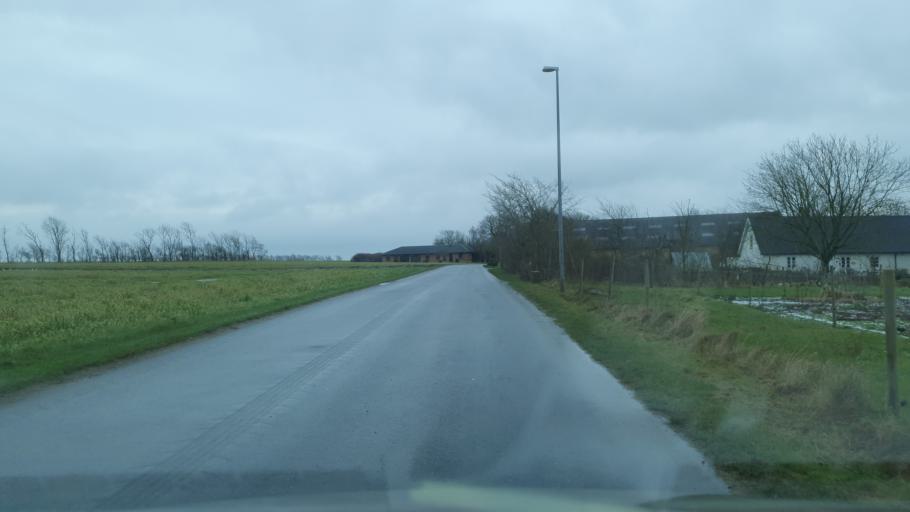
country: DK
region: North Denmark
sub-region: Jammerbugt Kommune
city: Fjerritslev
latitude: 57.1119
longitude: 9.1280
